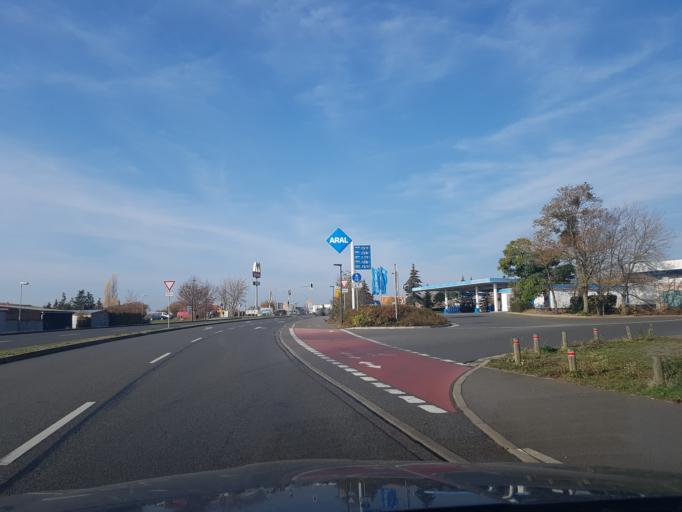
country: DE
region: Saxony
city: Zinna
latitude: 51.5610
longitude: 12.9742
